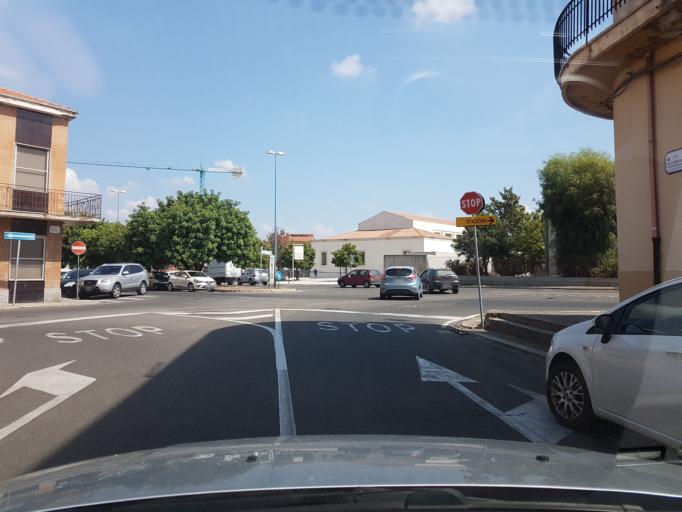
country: IT
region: Sardinia
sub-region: Provincia di Oristano
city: Oristano
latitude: 39.9066
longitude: 8.5997
